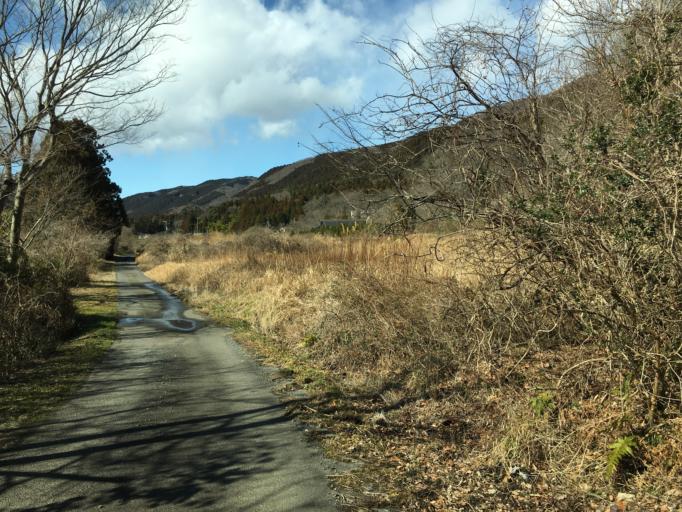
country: JP
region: Fukushima
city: Iwaki
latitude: 37.0072
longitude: 140.7953
